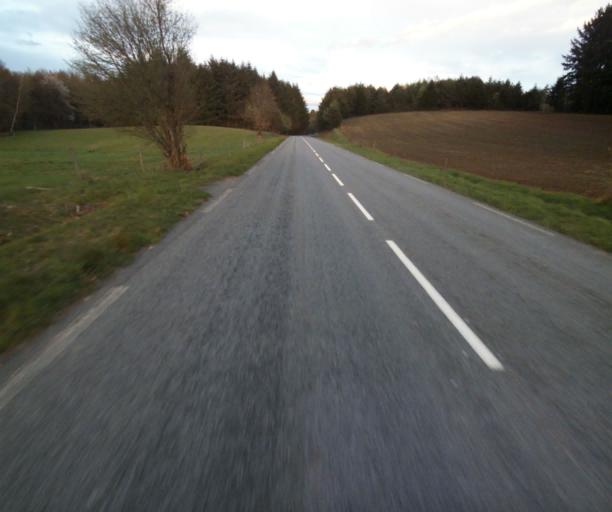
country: FR
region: Limousin
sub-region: Departement de la Correze
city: Laguenne
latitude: 45.2869
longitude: 1.8557
